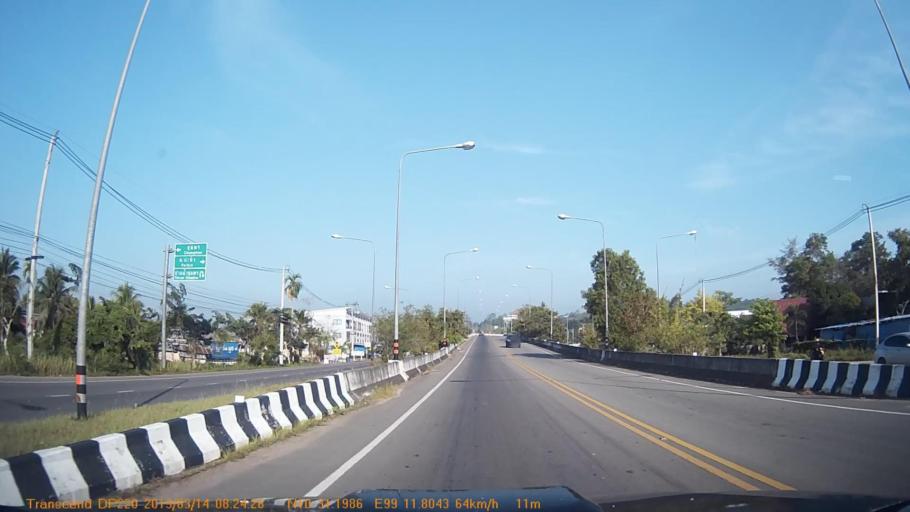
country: TH
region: Chumphon
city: Chumphon
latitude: 10.5201
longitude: 99.1966
